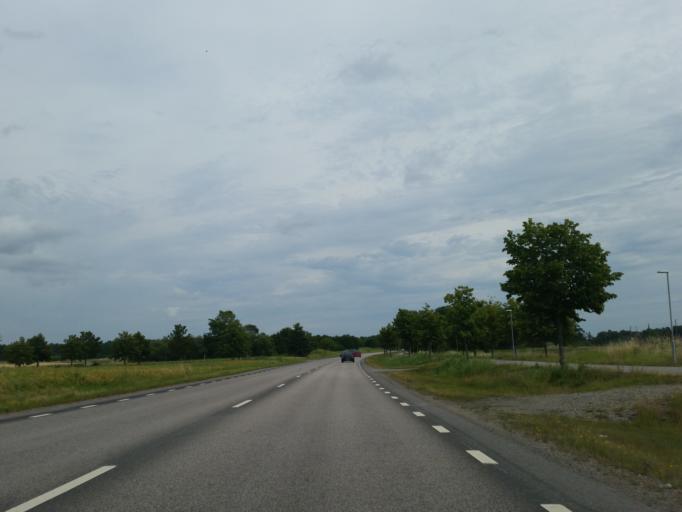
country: SE
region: Soedermanland
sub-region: Strangnas Kommun
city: Mariefred
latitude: 59.2554
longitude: 17.1844
